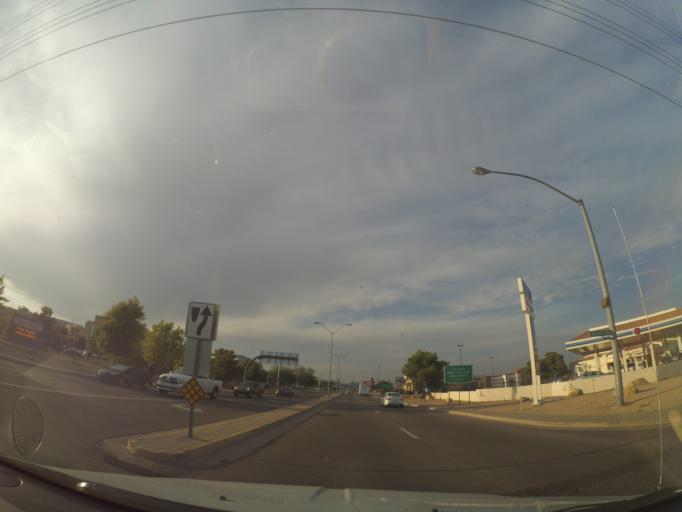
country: US
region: Arizona
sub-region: Mohave County
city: Kingman
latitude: 35.2187
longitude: -114.0356
